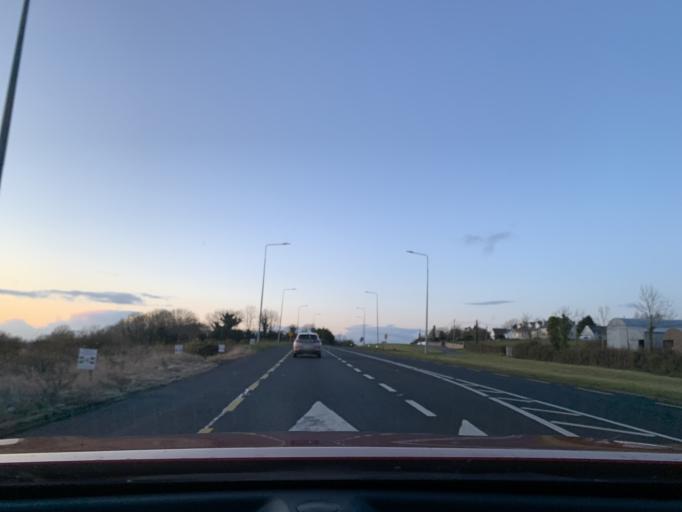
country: IE
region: Connaught
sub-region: County Leitrim
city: Carrick-on-Shannon
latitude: 53.8835
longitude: -7.9381
